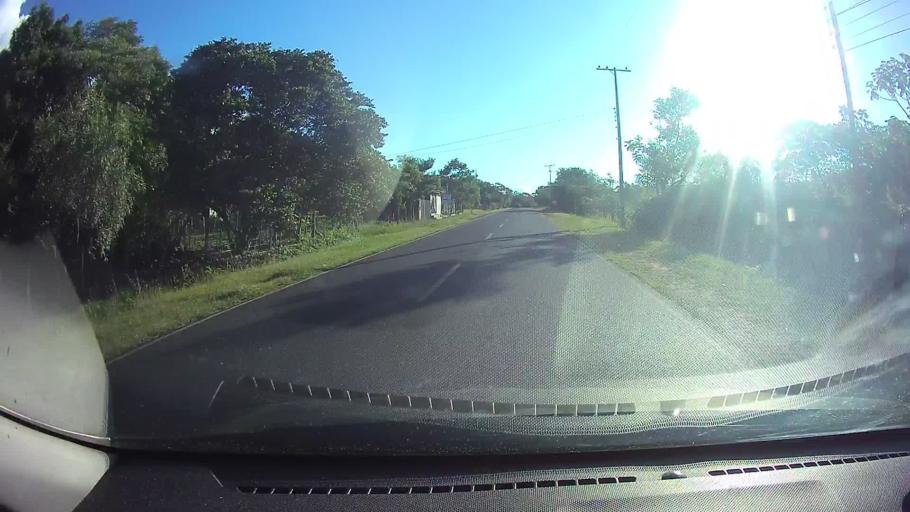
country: PY
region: Cordillera
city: Emboscada
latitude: -25.1688
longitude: -57.2748
